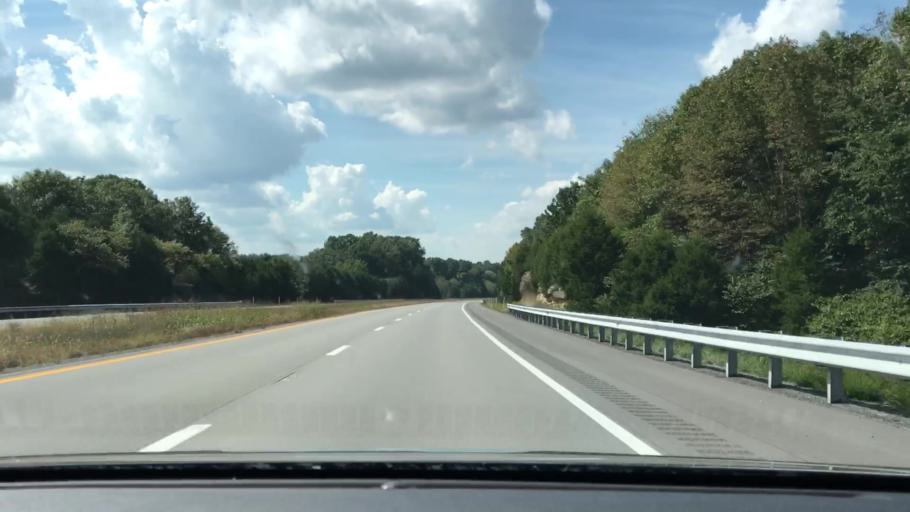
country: US
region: Kentucky
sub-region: Metcalfe County
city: Edmonton
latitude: 37.0287
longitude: -85.4888
